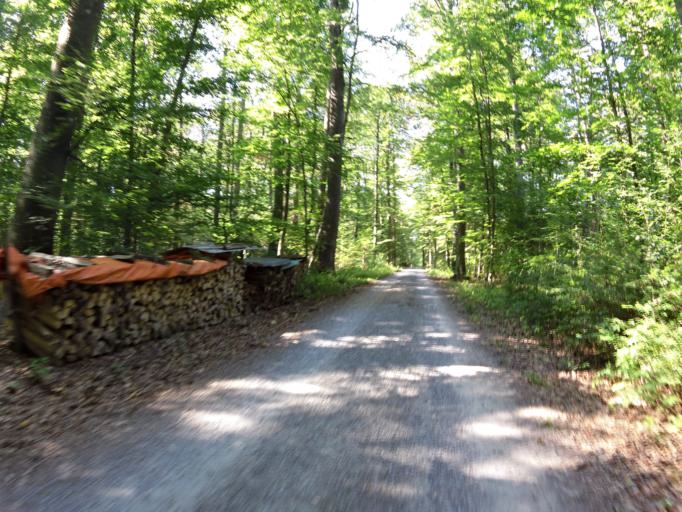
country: DE
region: Bavaria
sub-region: Regierungsbezirk Unterfranken
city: Margetshochheim
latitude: 49.8575
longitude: 9.8770
